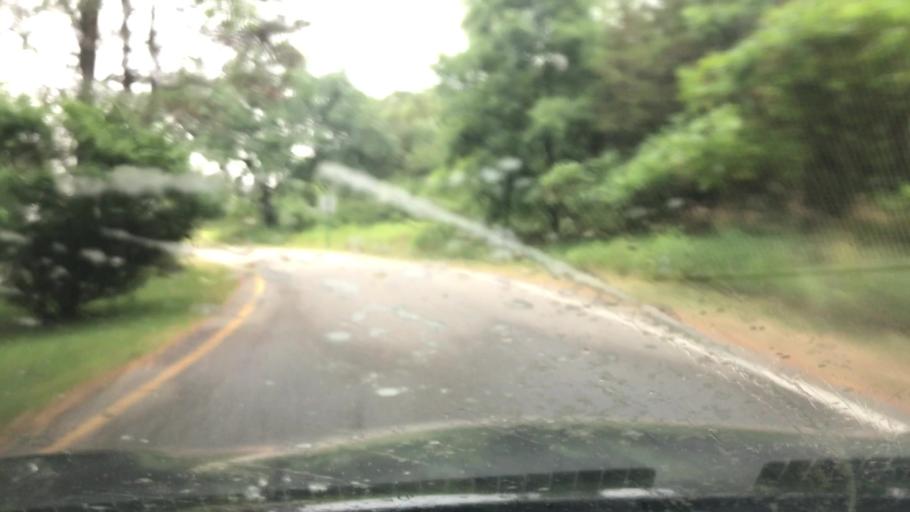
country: US
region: Michigan
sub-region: Oakland County
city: South Lyon
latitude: 42.5106
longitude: -83.6847
